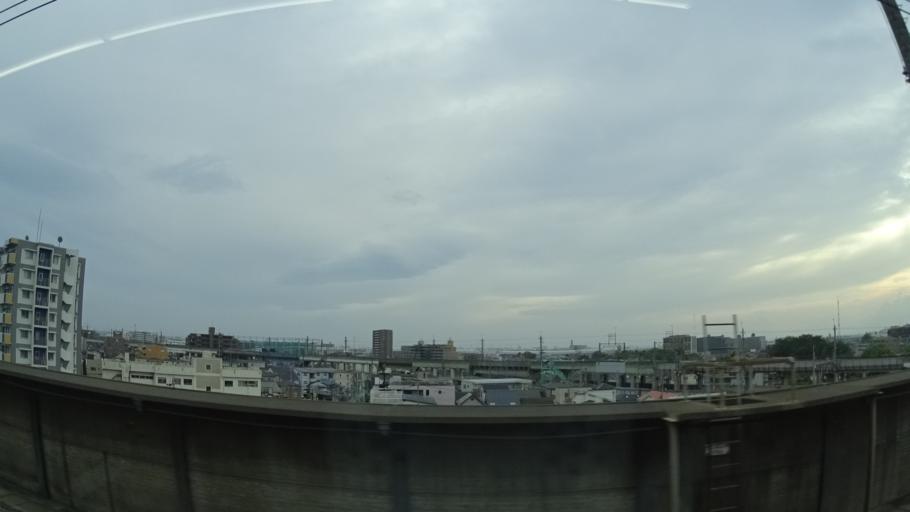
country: JP
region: Saitama
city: Yono
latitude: 35.8534
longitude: 139.6377
